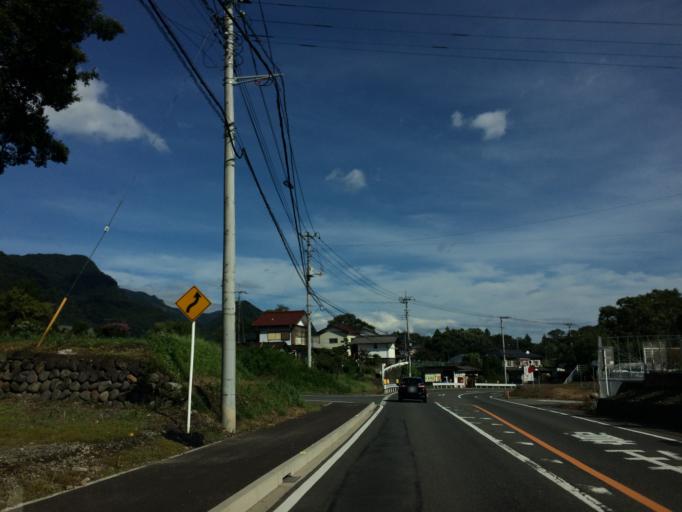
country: JP
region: Gunma
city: Nakanojomachi
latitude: 36.5720
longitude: 138.8676
